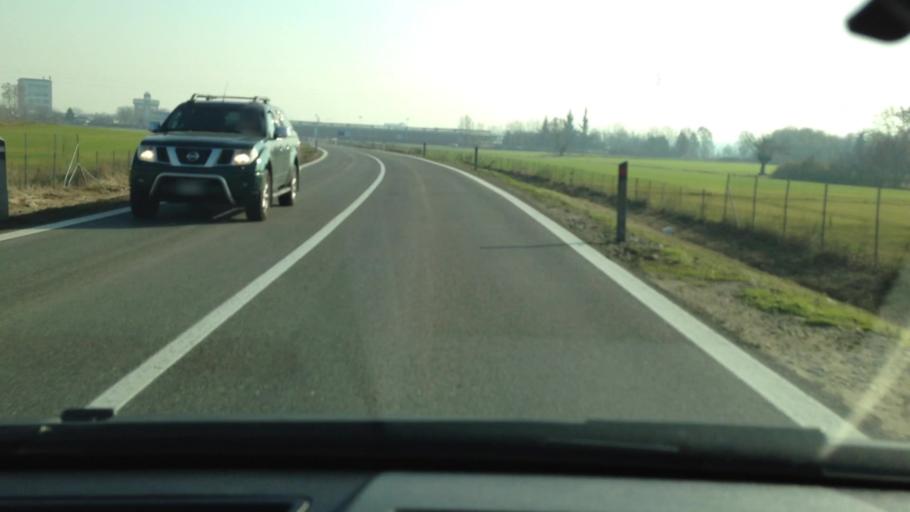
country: IT
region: Piedmont
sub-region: Provincia di Alessandria
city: Quattordio
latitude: 44.9028
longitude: 8.4161
